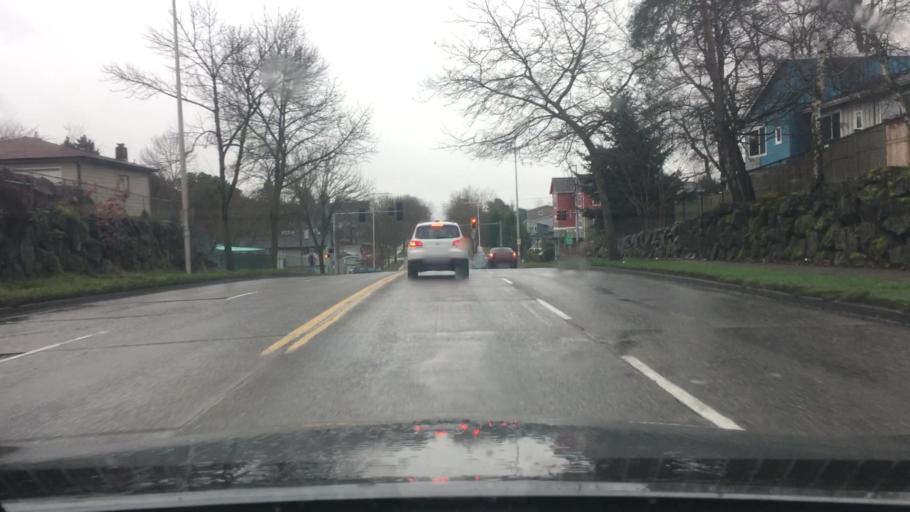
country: US
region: Washington
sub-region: King County
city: White Center
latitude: 47.5173
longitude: -122.3467
